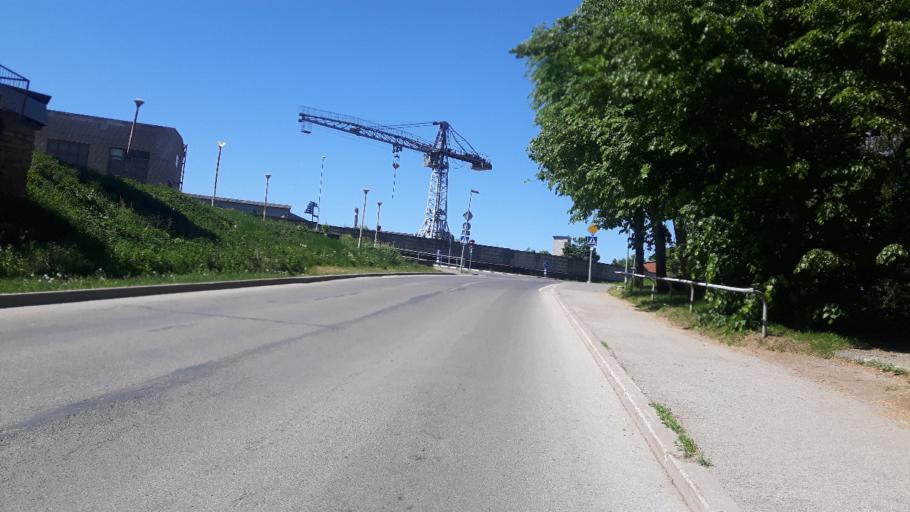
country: EE
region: Ida-Virumaa
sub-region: Sillamaee linn
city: Sillamae
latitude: 59.3991
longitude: 27.7495
